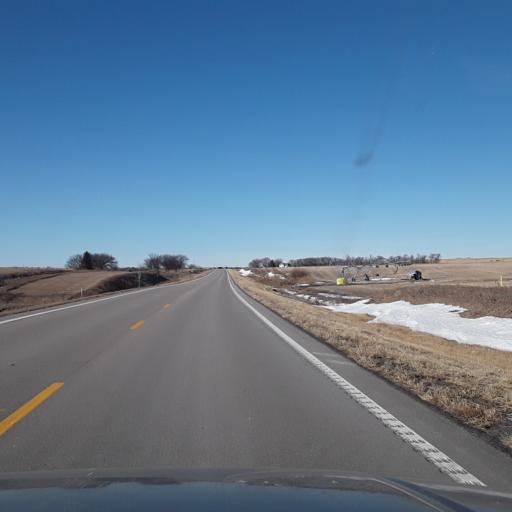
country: US
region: Nebraska
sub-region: Dawson County
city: Cozad
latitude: 40.6723
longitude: -100.1064
